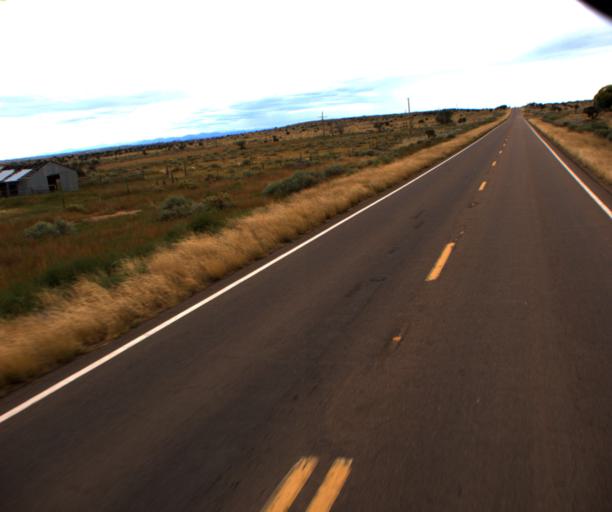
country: US
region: Arizona
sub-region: Navajo County
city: Snowflake
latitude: 34.5595
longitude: -110.0813
